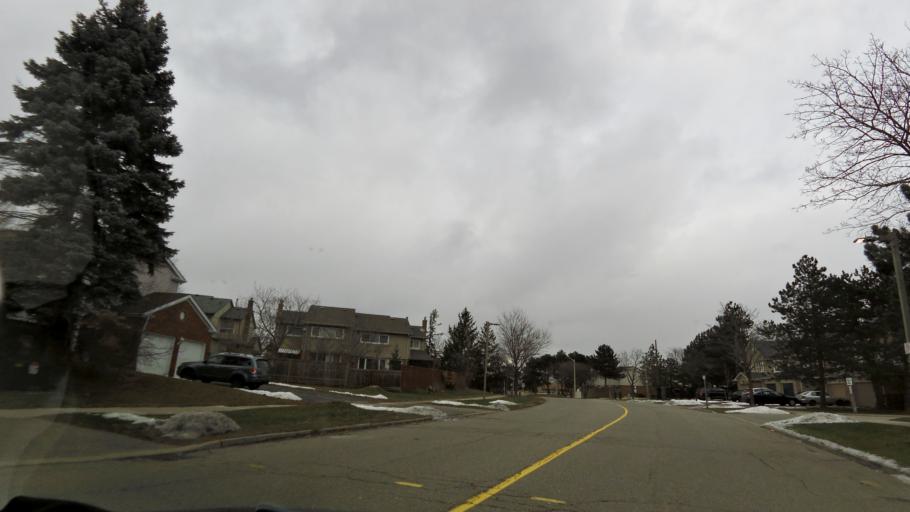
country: CA
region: Ontario
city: Mississauga
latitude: 43.5461
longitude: -79.7008
